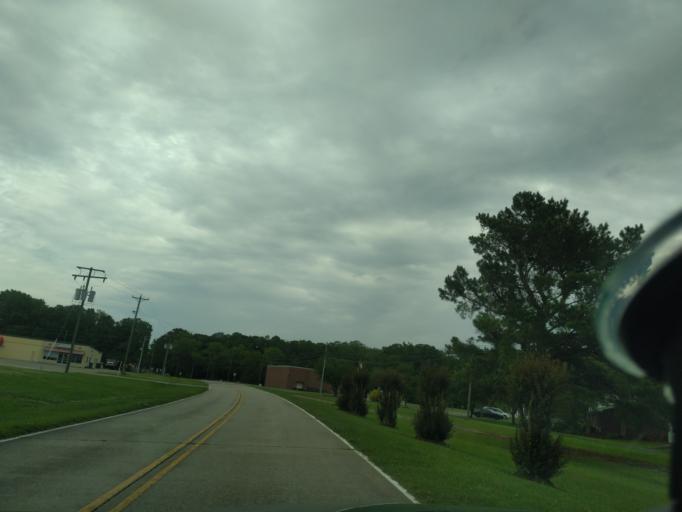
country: US
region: North Carolina
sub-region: Washington County
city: Plymouth
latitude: 35.8743
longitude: -76.6212
